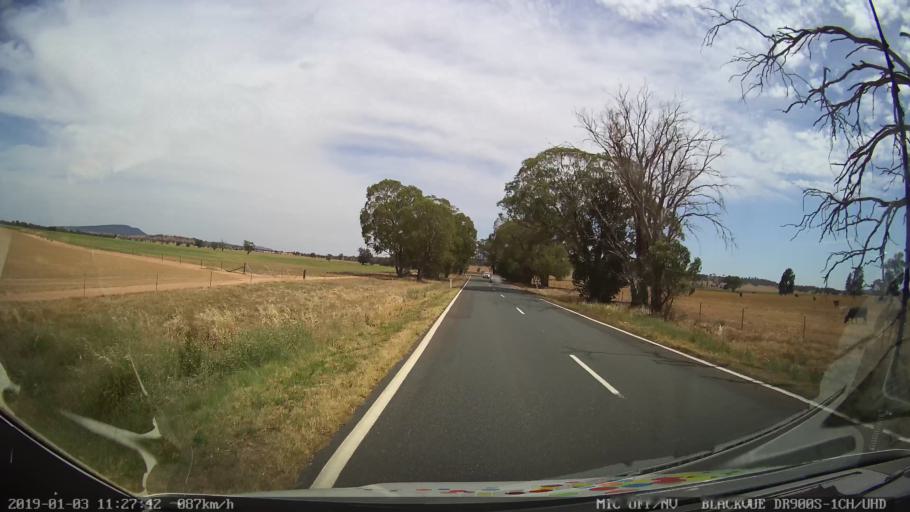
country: AU
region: New South Wales
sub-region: Weddin
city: Grenfell
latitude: -34.0095
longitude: 148.2168
